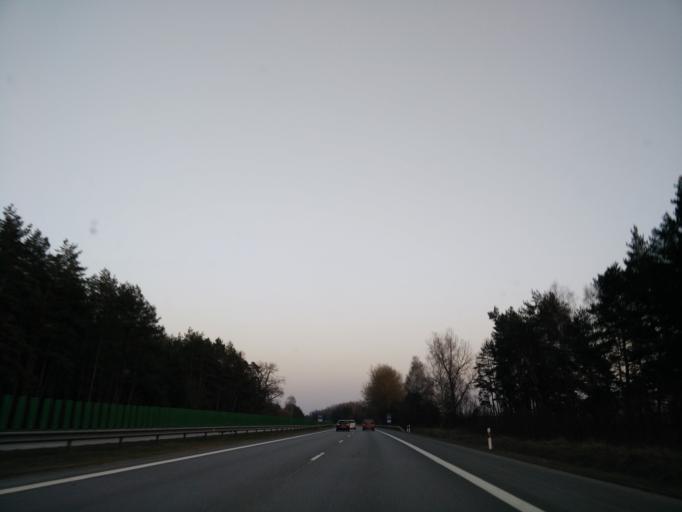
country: LT
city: Lentvaris
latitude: 54.6998
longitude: 25.0117
